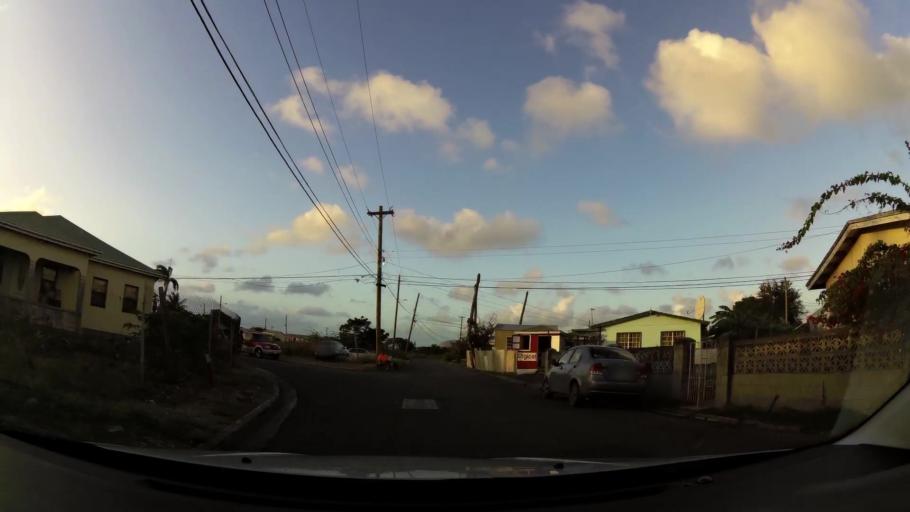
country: AG
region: Saint John
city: Saint John's
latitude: 17.1328
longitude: -61.8392
